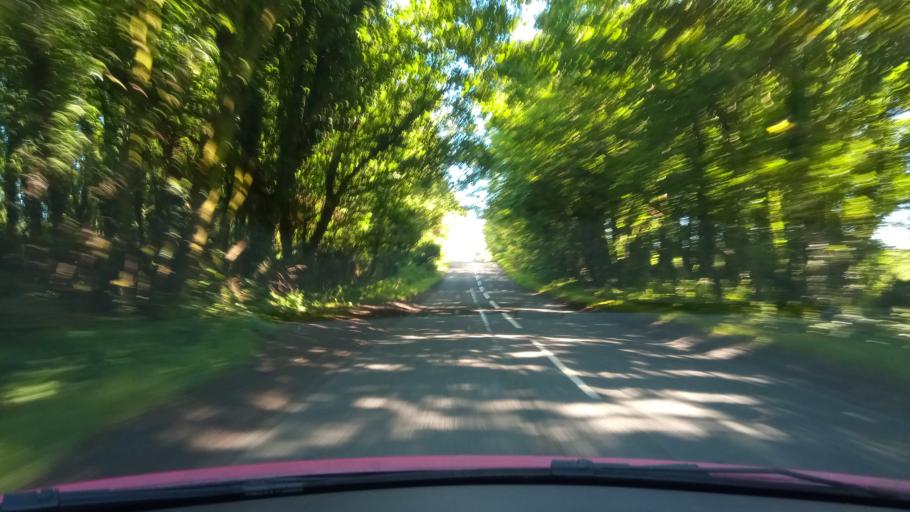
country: GB
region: Scotland
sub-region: East Lothian
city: East Linton
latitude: 56.0094
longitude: -2.6293
